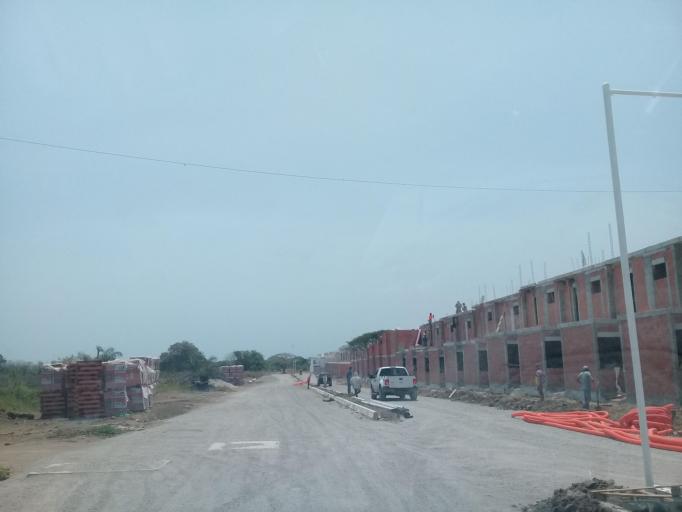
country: MX
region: Veracruz
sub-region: Veracruz
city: Hacienda Sotavento
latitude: 19.1441
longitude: -96.1758
